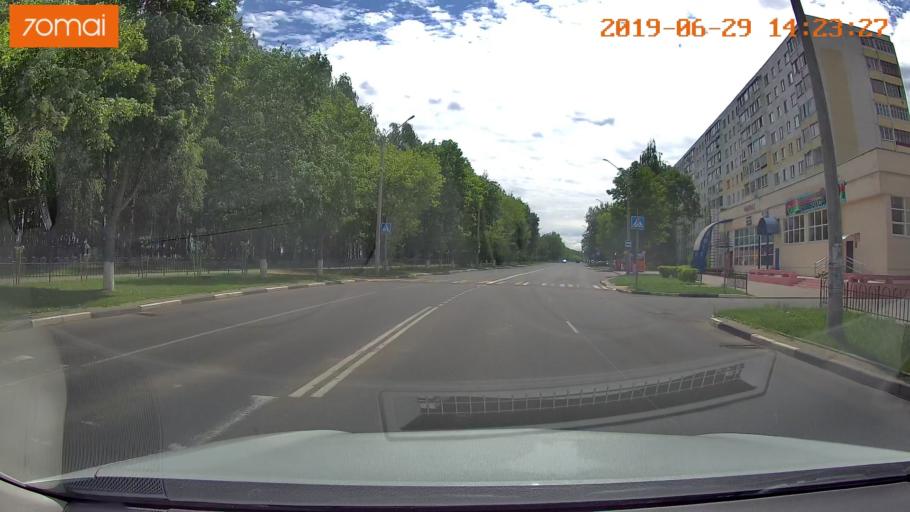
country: BY
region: Minsk
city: Salihorsk
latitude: 52.7857
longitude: 27.5542
